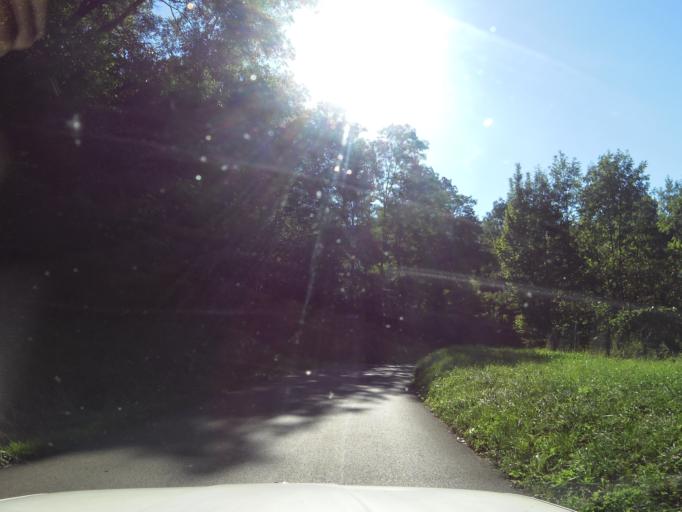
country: FR
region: Rhone-Alpes
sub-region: Departement de l'Ain
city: Vaux-en-Bugey
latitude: 45.9401
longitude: 5.3655
